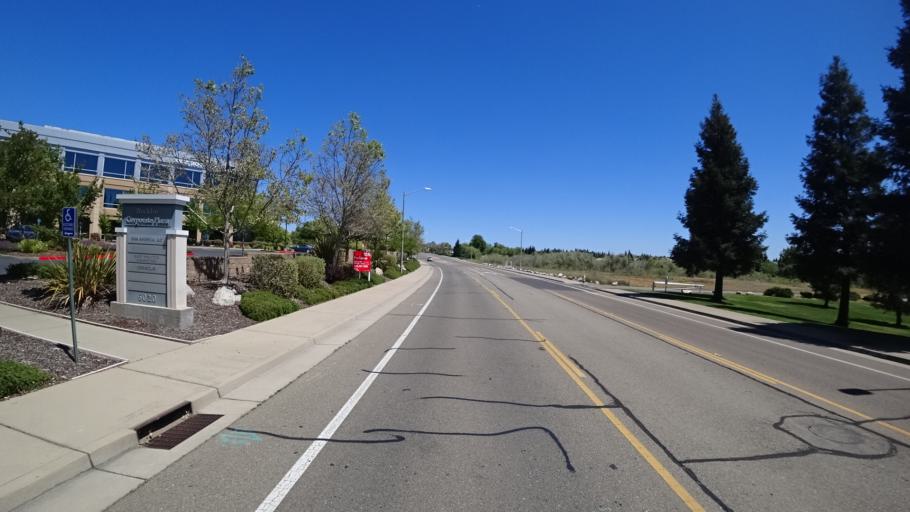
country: US
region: California
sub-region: Placer County
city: Rocklin
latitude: 38.8102
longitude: -121.2877
